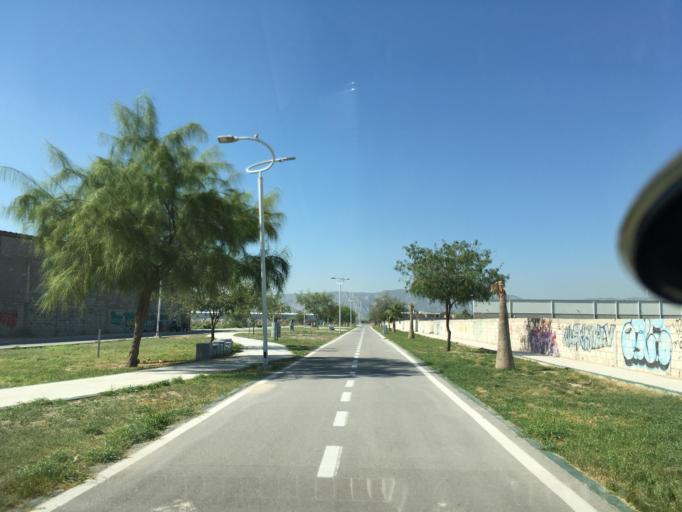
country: MX
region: Coahuila
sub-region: Torreon
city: Fraccionamiento la Noria
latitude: 25.5278
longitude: -103.3749
